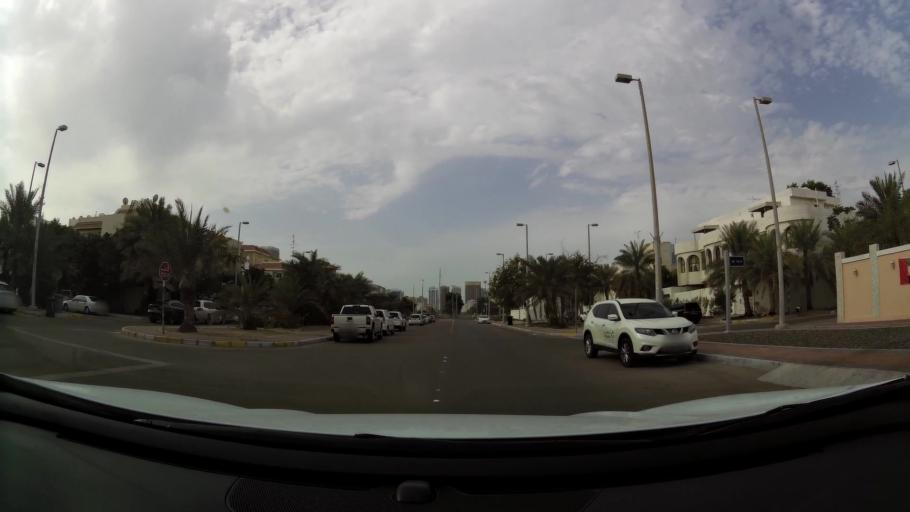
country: AE
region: Abu Dhabi
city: Abu Dhabi
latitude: 24.4633
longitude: 54.3522
